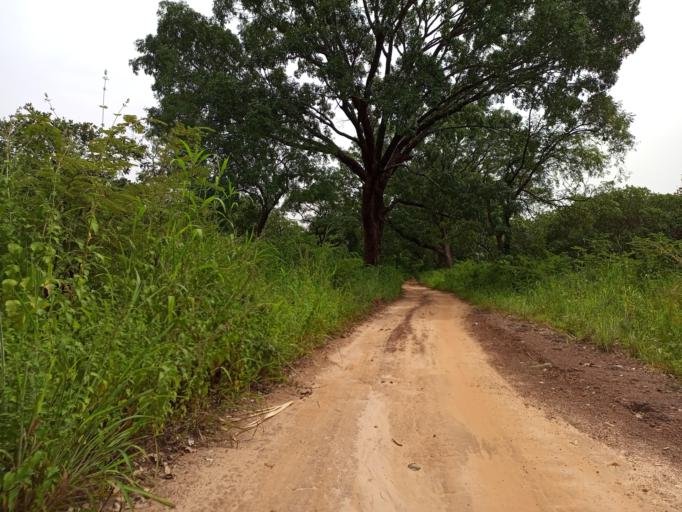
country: GW
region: Oio
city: Farim
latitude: 12.4245
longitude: -15.4004
